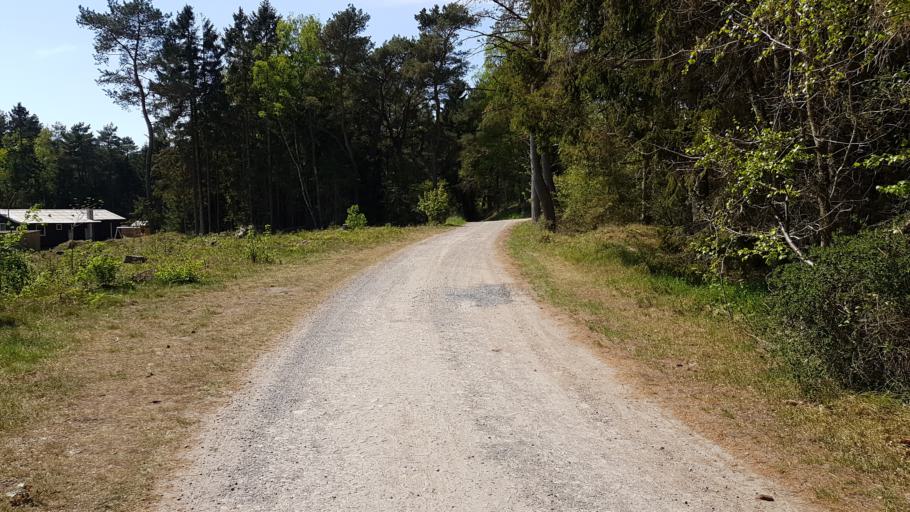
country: DK
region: Capital Region
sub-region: Bornholm Kommune
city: Nexo
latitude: 55.0011
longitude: 15.0830
